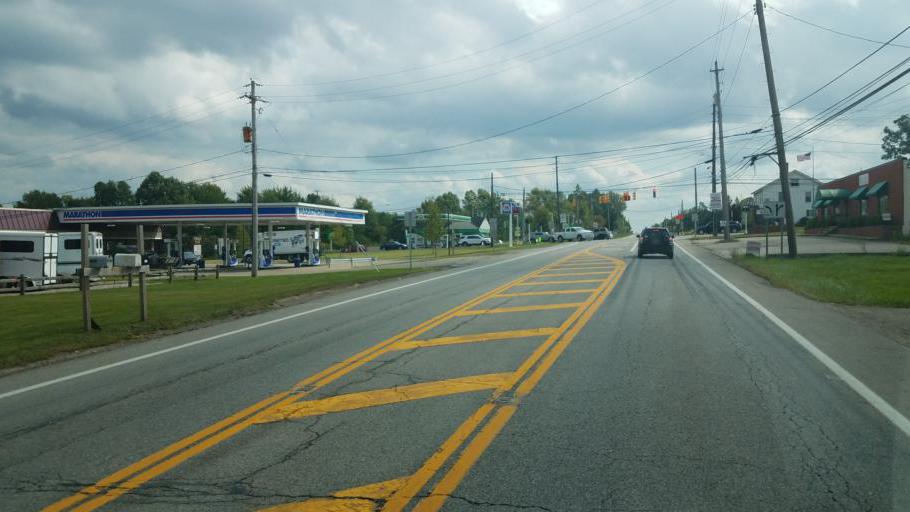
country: US
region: Ohio
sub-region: Geauga County
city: Burton
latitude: 41.4718
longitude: -81.1937
